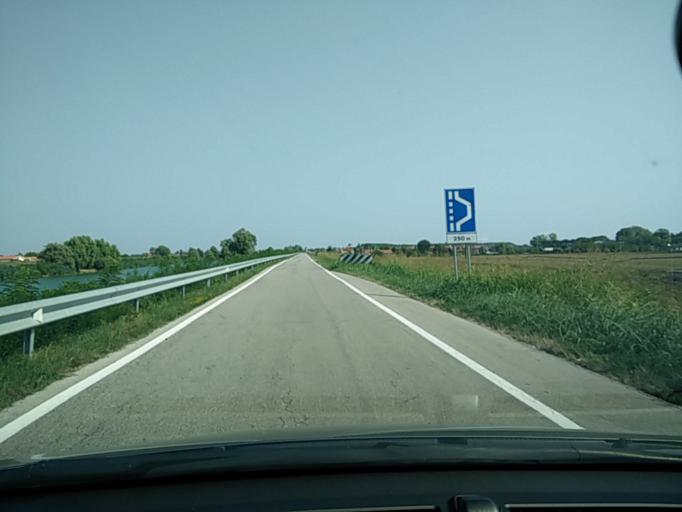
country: IT
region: Veneto
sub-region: Provincia di Venezia
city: La Salute di Livenza
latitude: 45.6521
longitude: 12.8067
